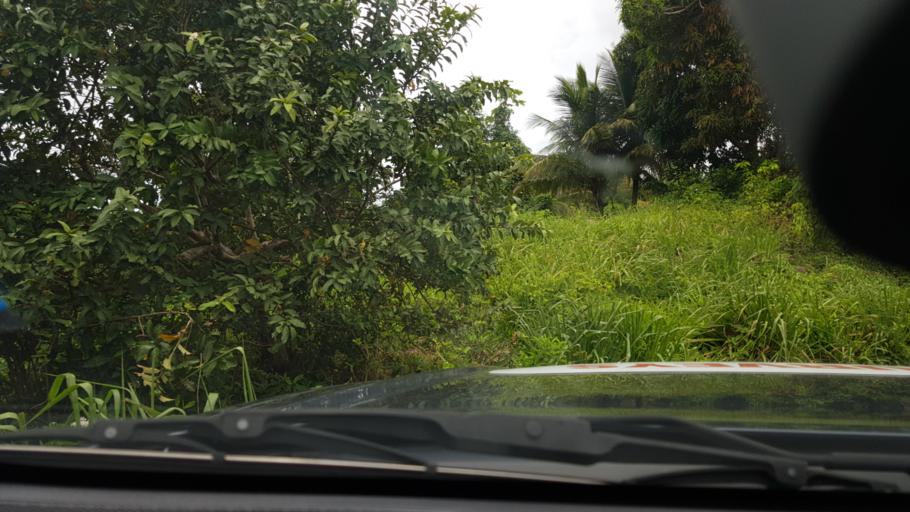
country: LC
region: Castries Quarter
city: Bisee
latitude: 14.0075
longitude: -60.9360
